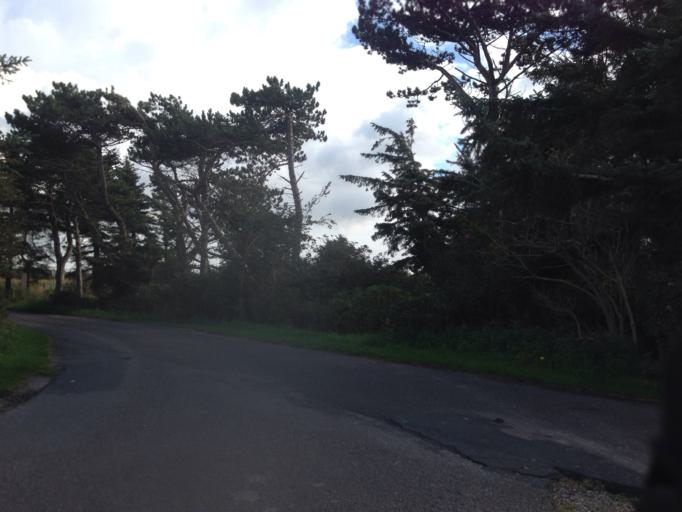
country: DE
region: Schleswig-Holstein
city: Utersum
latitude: 54.7168
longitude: 8.3976
